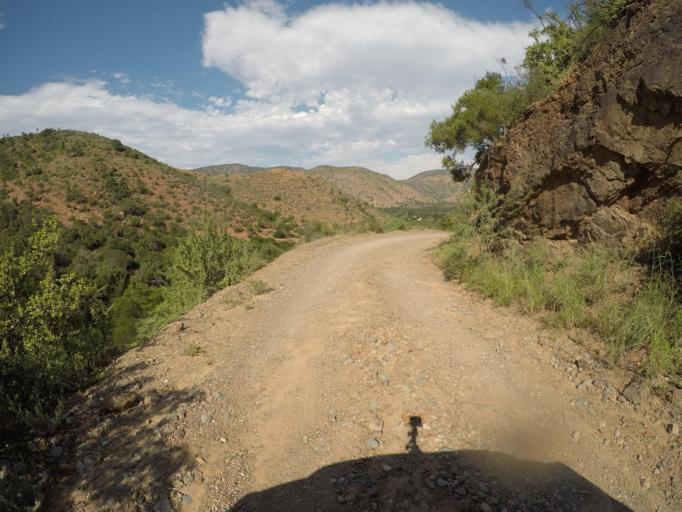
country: ZA
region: Eastern Cape
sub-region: Cacadu District Municipality
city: Kareedouw
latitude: -33.6576
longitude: 24.4012
